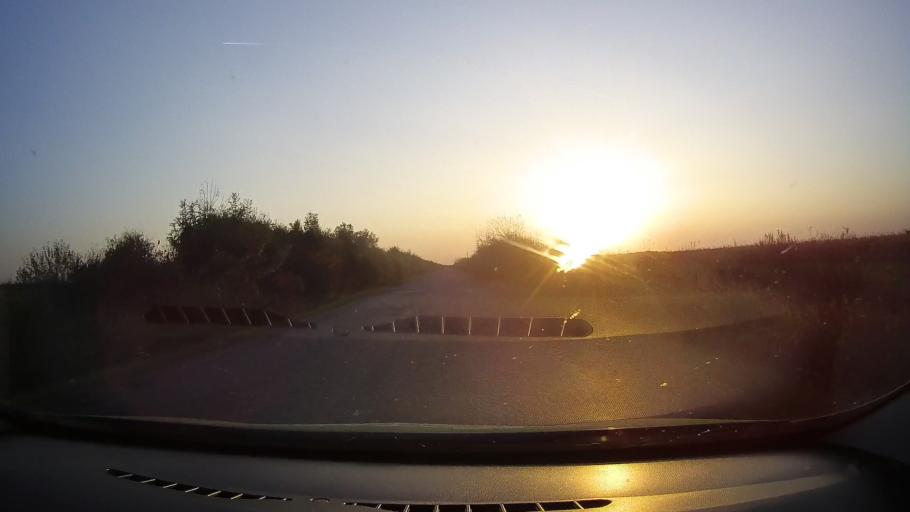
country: RO
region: Arad
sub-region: Comuna Sicula
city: Sicula
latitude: 46.4212
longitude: 21.7443
